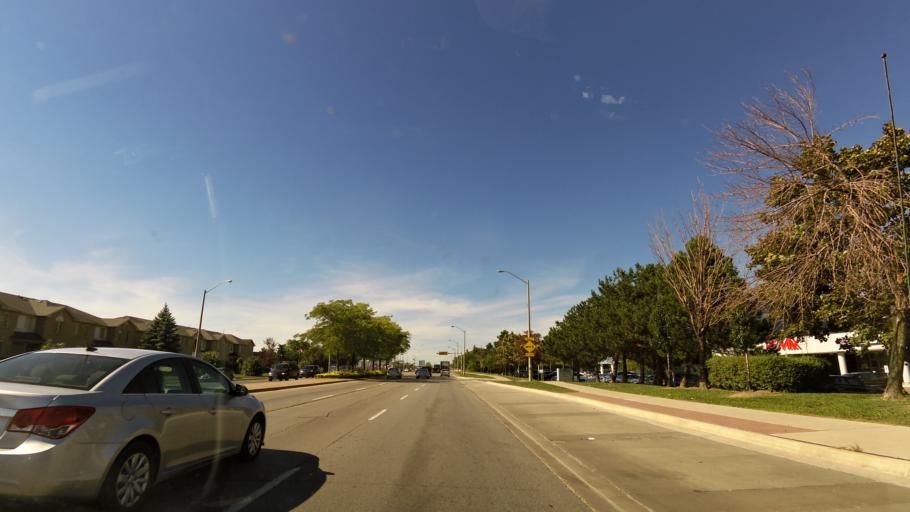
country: CA
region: Ontario
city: Brampton
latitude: 43.6622
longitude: -79.7279
